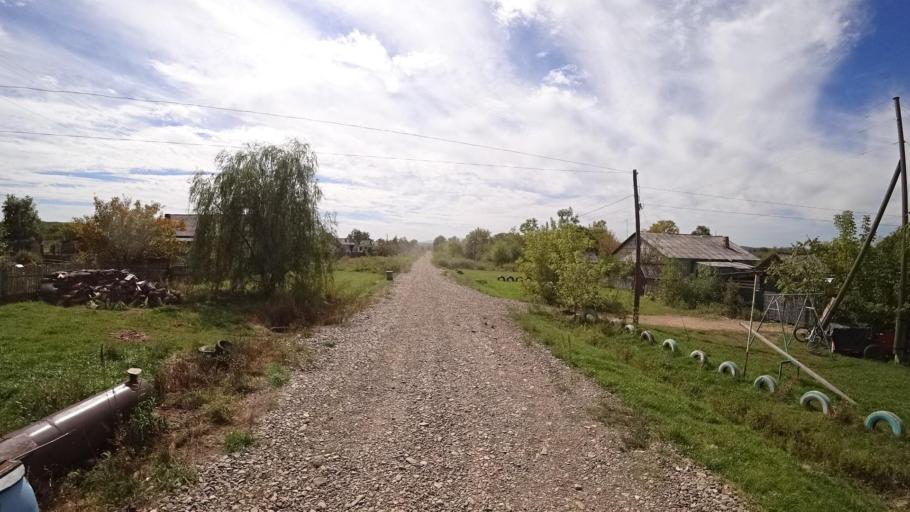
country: RU
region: Primorskiy
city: Yakovlevka
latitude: 44.6435
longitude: 133.6027
